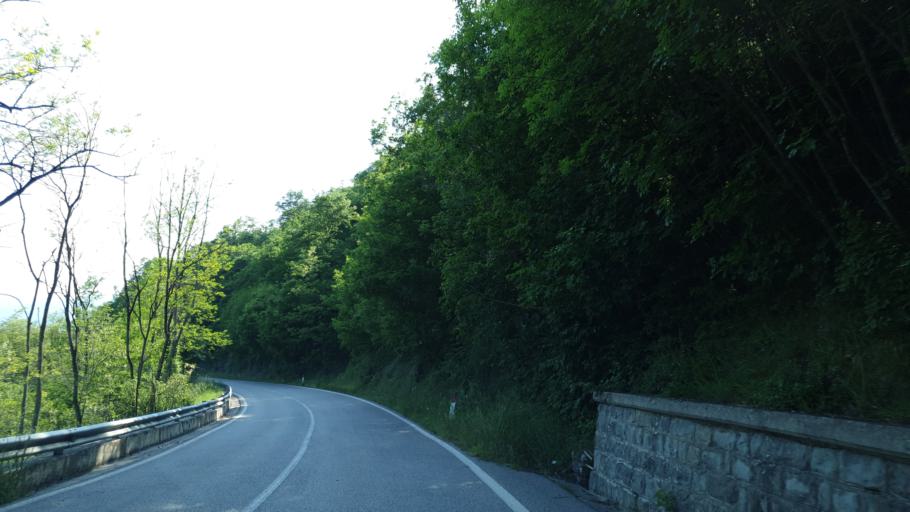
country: IT
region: Tuscany
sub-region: Province of Arezzo
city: Soci
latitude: 43.7604
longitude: 11.8324
